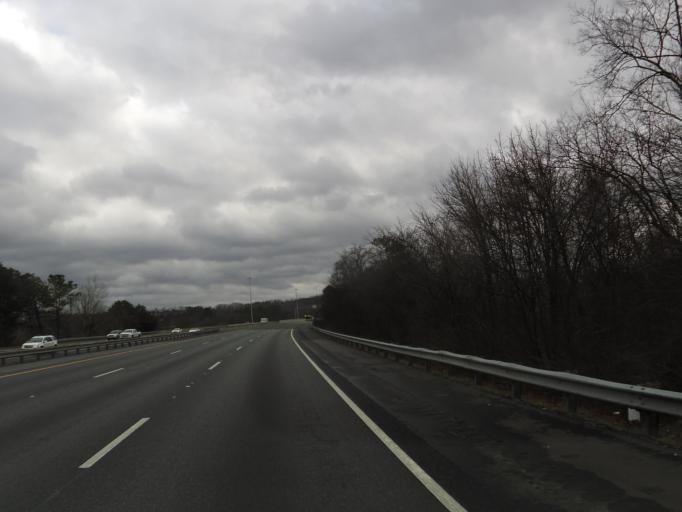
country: US
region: Georgia
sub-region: Whitfield County
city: Dalton
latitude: 34.7999
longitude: -85.0067
